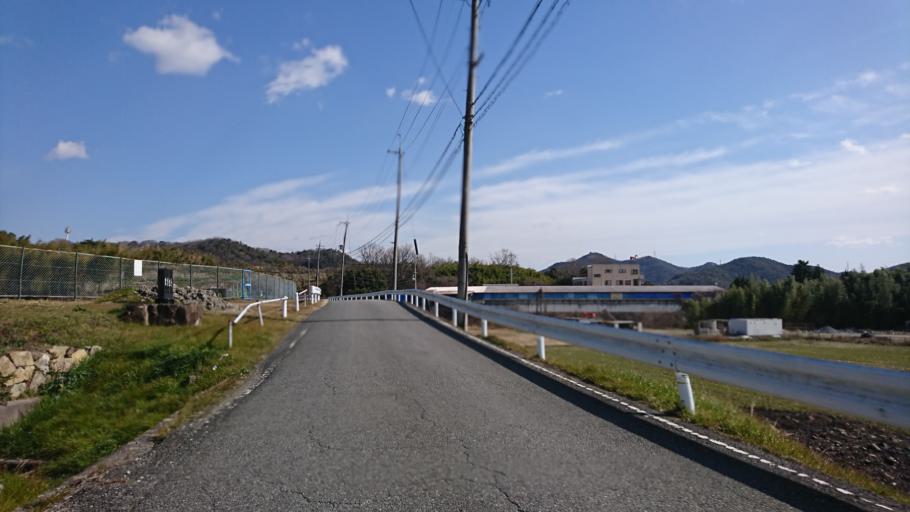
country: JP
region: Hyogo
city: Kakogawacho-honmachi
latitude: 34.8206
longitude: 134.8297
